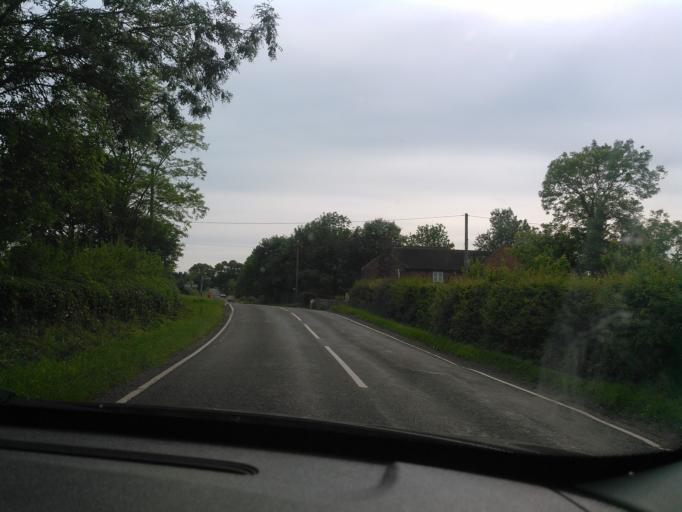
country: GB
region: England
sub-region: Shropshire
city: Astley
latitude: 52.7377
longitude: -2.6641
